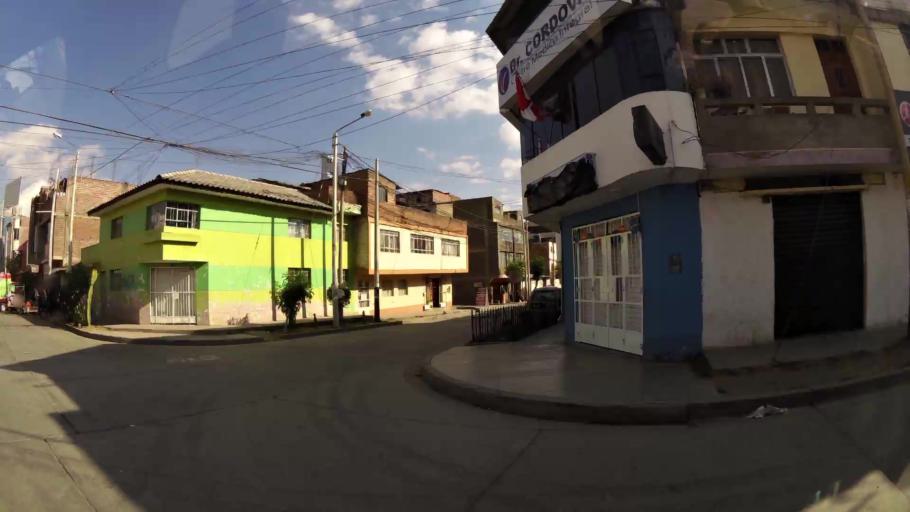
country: PE
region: Junin
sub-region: Provincia de Huancayo
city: El Tambo
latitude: -12.0642
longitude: -75.2174
